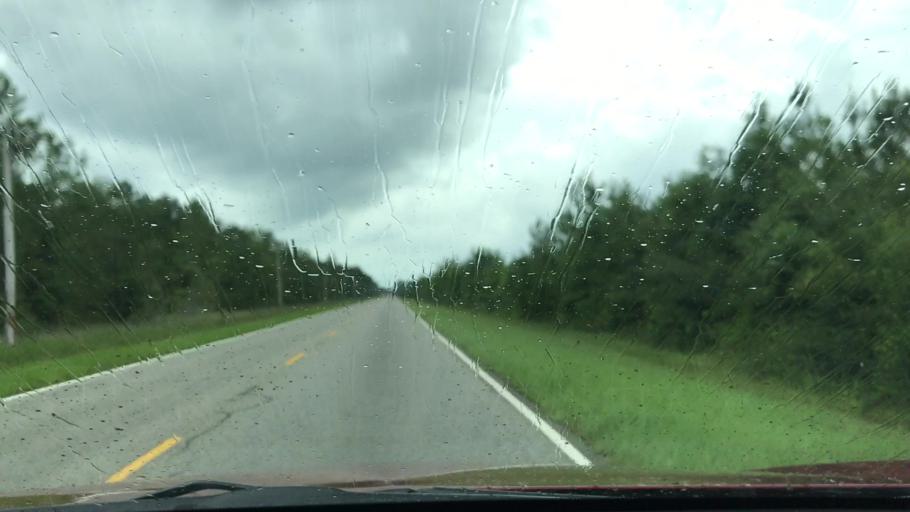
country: US
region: South Carolina
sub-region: Georgetown County
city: Georgetown
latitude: 33.5183
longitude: -79.2473
